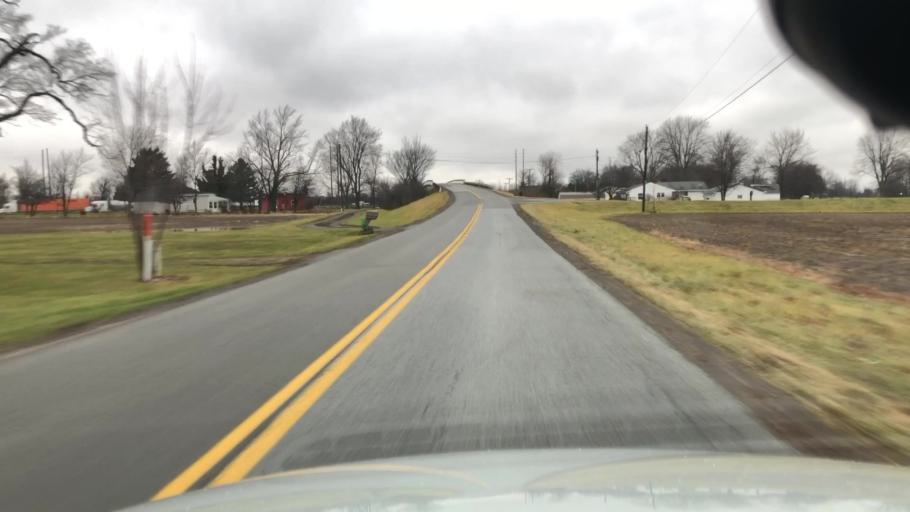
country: US
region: Ohio
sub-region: Allen County
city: Lima
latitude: 40.8060
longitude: -84.0131
